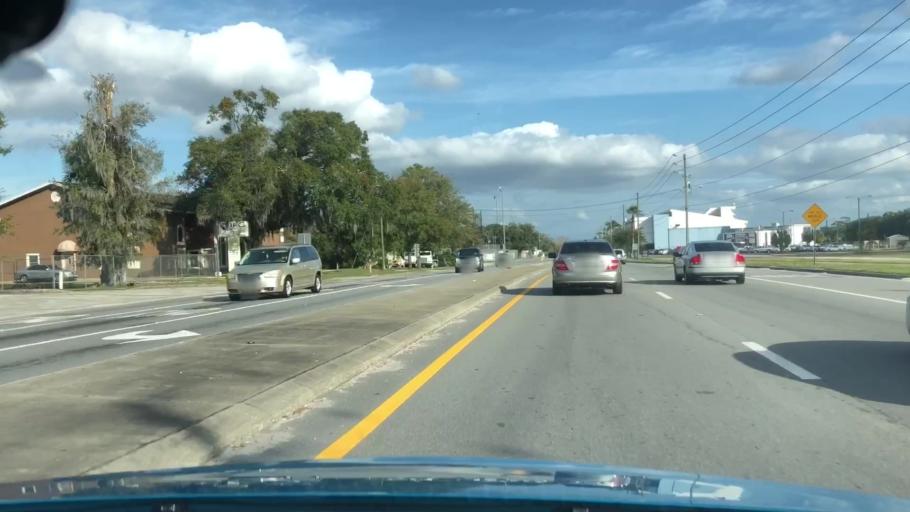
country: US
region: Florida
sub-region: Seminole County
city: Casselberry
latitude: 28.6823
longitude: -81.3468
